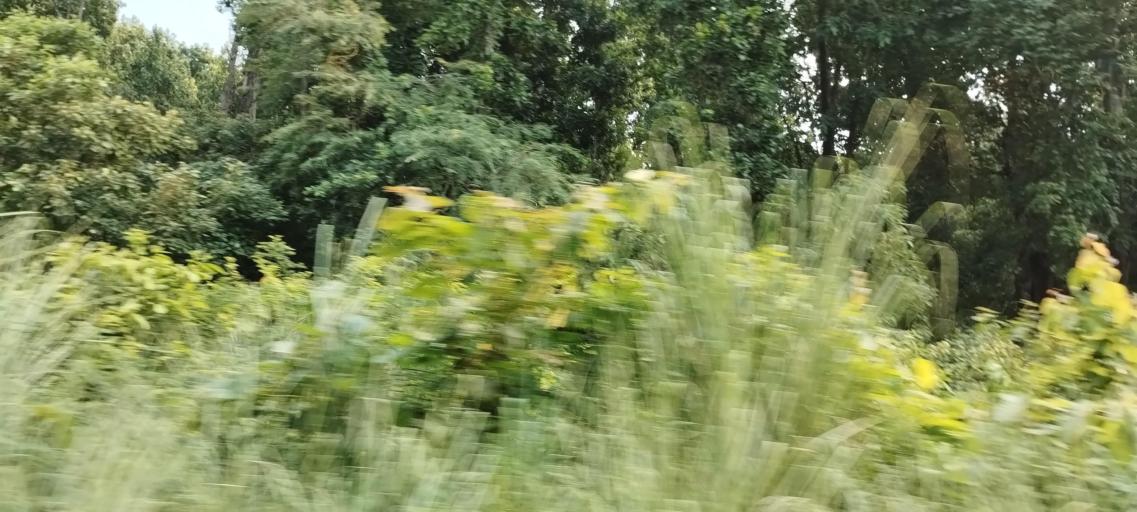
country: NP
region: Mid Western
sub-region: Bheri Zone
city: Bardiya
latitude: 28.4305
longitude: 81.3553
